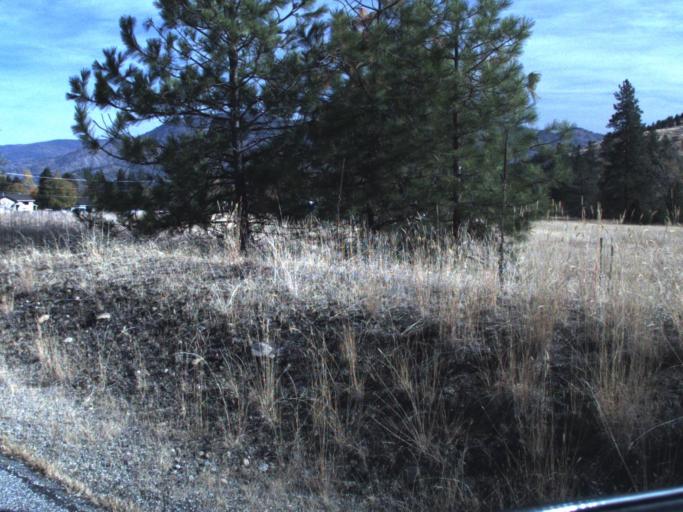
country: CA
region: British Columbia
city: Grand Forks
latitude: 48.9980
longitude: -118.5045
